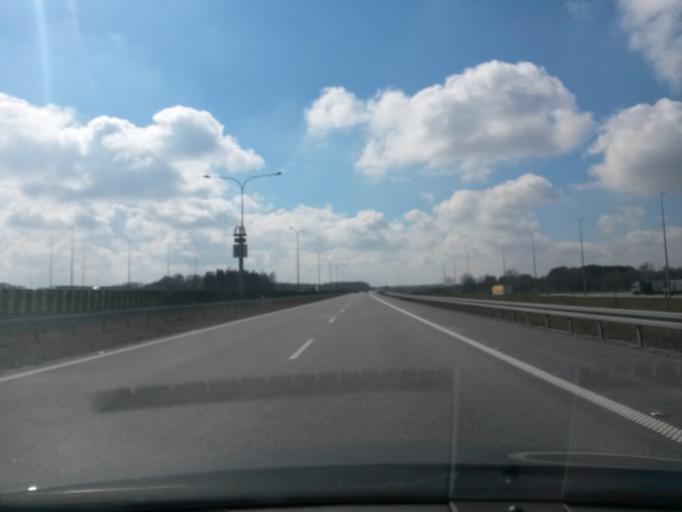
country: PL
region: Lodz Voivodeship
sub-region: powiat Lowicki
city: Bobrowniki
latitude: 52.0287
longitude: 20.0044
